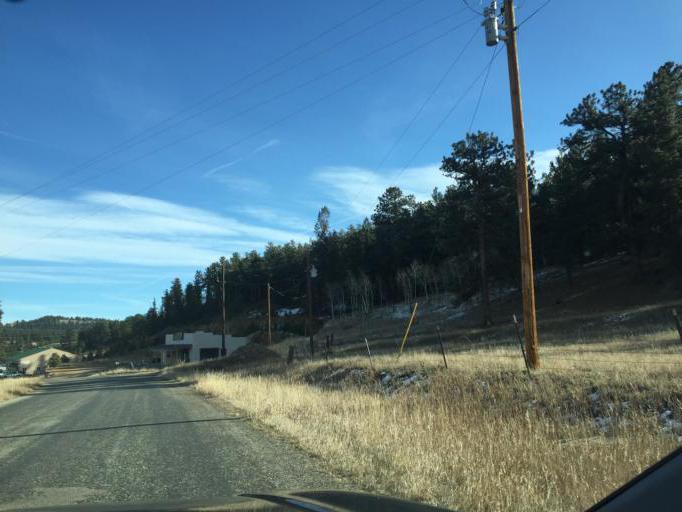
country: US
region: Colorado
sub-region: Jefferson County
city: Evergreen
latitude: 39.4379
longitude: -105.4544
